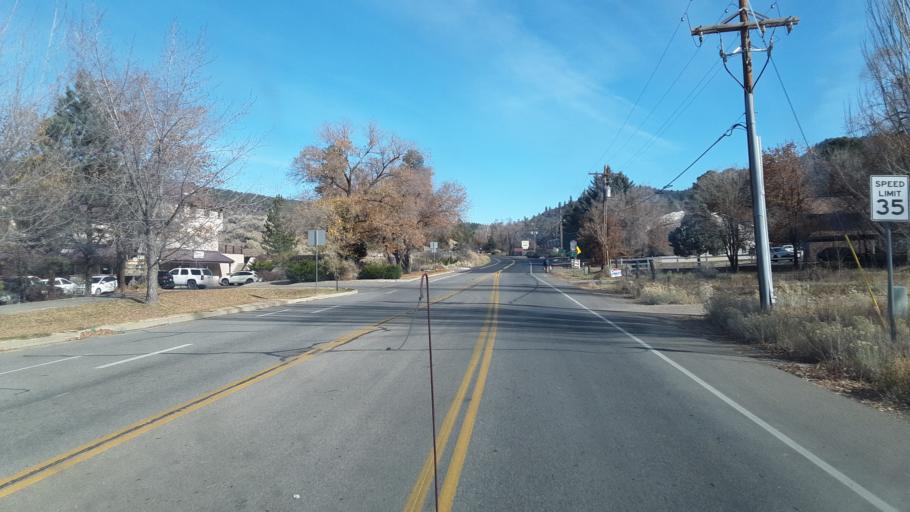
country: US
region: Colorado
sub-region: La Plata County
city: Durango
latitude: 37.2977
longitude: -107.8481
